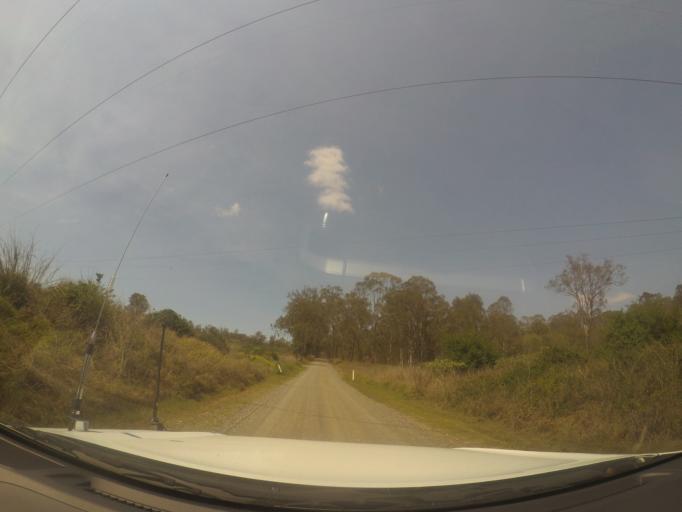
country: AU
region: Queensland
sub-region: Logan
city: North Maclean
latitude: -27.7735
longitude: 153.0383
